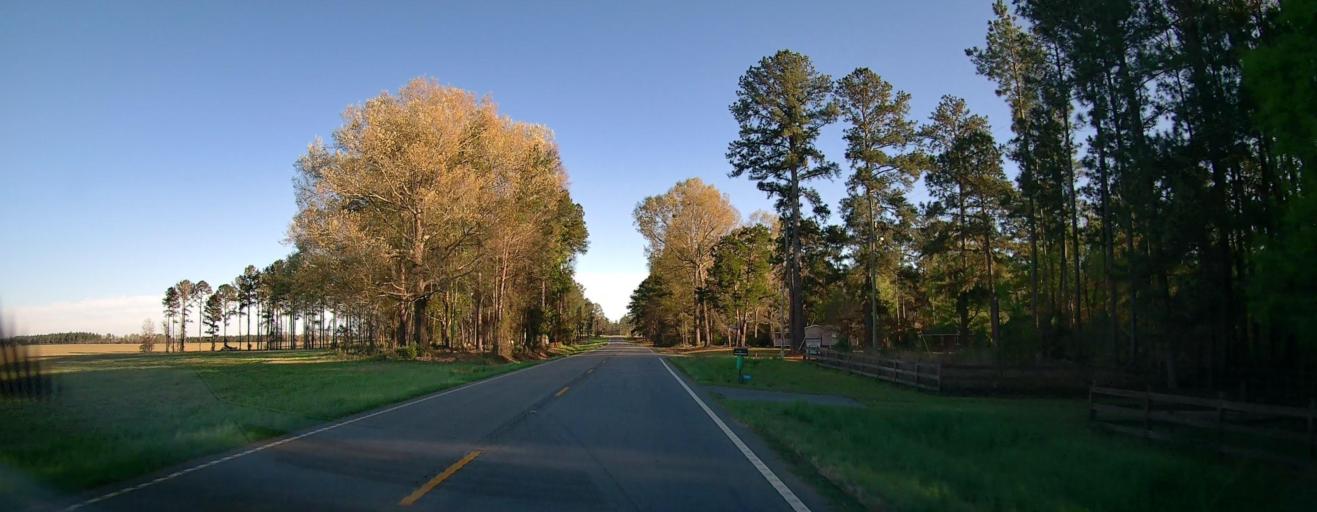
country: US
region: Georgia
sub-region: Pulaski County
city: Hawkinsville
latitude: 32.2159
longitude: -83.3845
